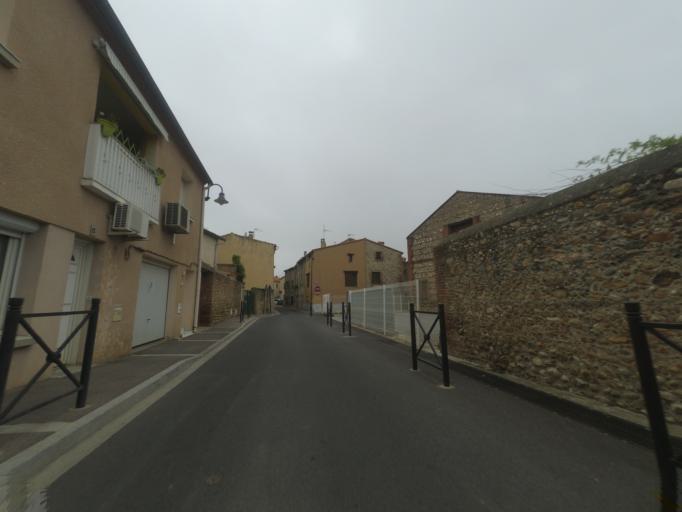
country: FR
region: Languedoc-Roussillon
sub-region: Departement des Pyrenees-Orientales
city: Villeneuve-la-Riviere
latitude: 42.6932
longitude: 2.8026
